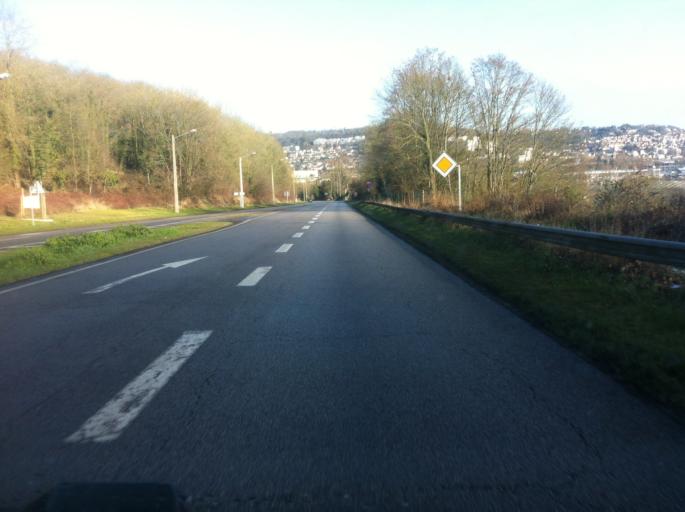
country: FR
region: Haute-Normandie
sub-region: Departement de la Seine-Maritime
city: Canteleu
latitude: 49.4451
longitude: 1.0424
